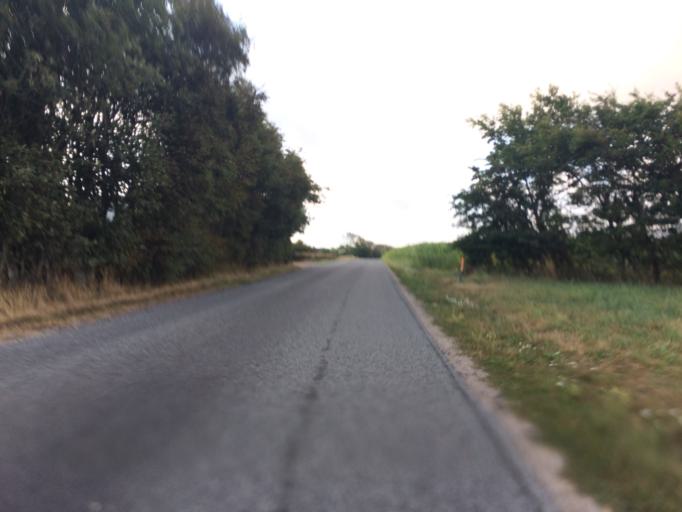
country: DK
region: Central Jutland
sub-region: Holstebro Kommune
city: Vinderup
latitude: 56.6161
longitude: 8.7617
